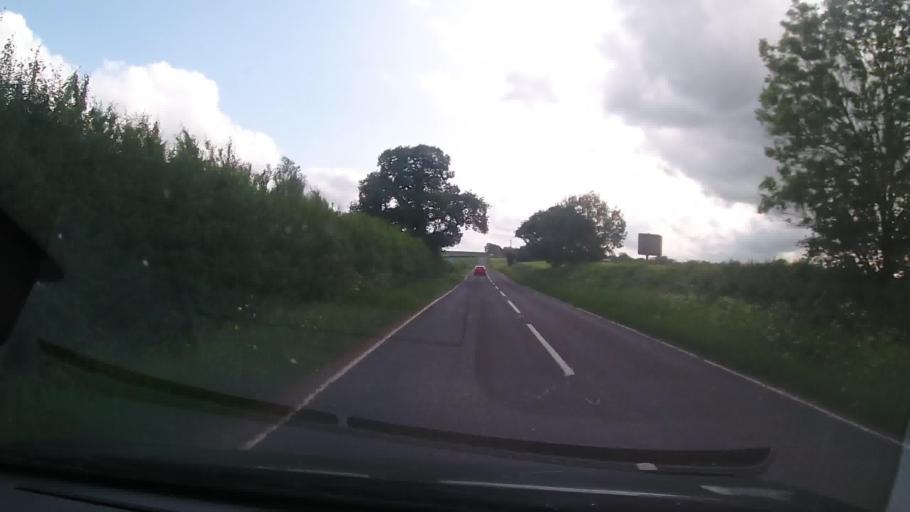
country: GB
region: England
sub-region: Shropshire
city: Clive
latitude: 52.8191
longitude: -2.7418
